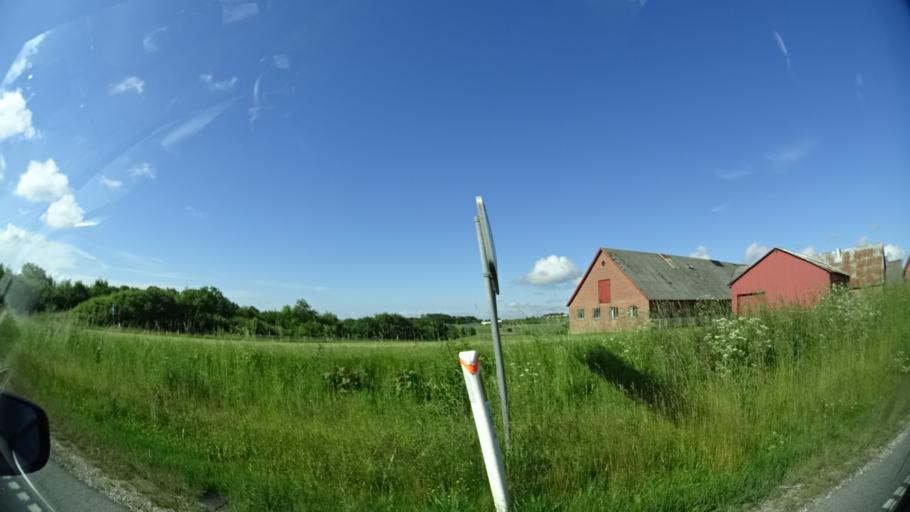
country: DK
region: Central Jutland
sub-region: Syddjurs Kommune
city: Ronde
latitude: 56.3158
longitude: 10.4262
